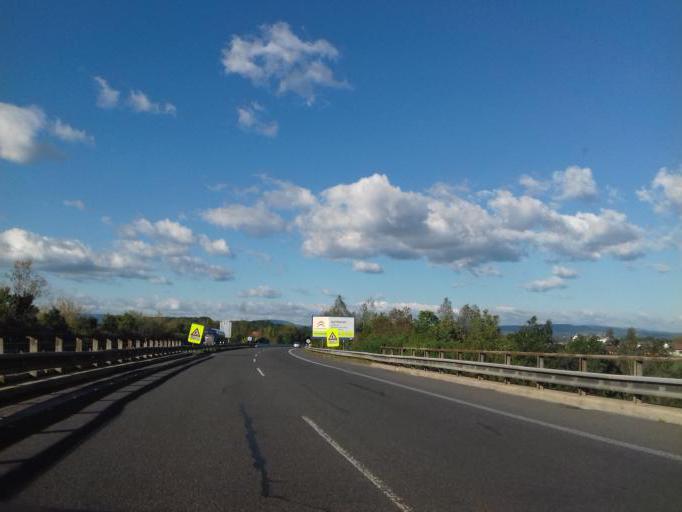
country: CZ
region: Central Bohemia
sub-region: Okres Mlada Boleslav
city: Zd'ar
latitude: 50.5505
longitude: 15.0434
